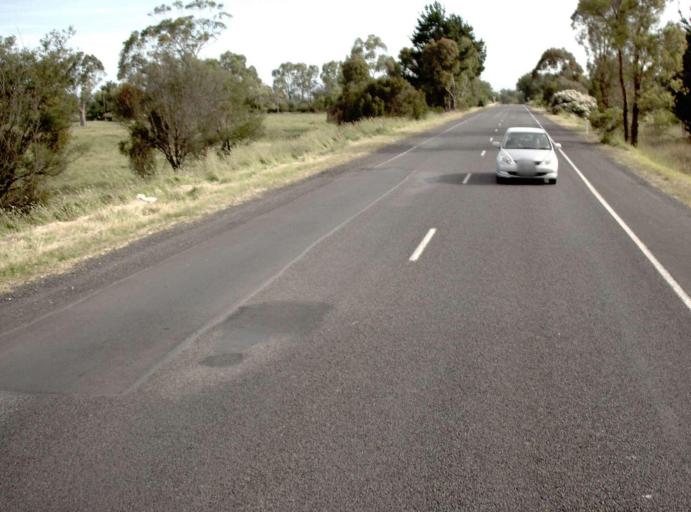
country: AU
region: Victoria
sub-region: Latrobe
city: Traralgon
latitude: -38.1502
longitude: 146.5546
